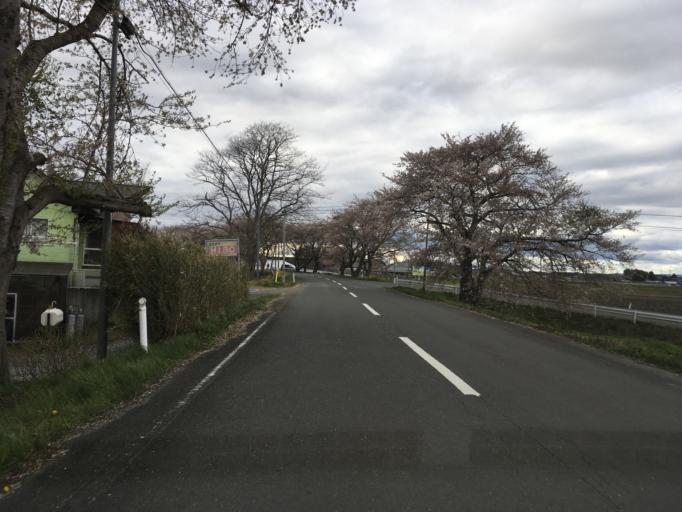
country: JP
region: Miyagi
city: Wakuya
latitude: 38.6459
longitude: 141.1784
